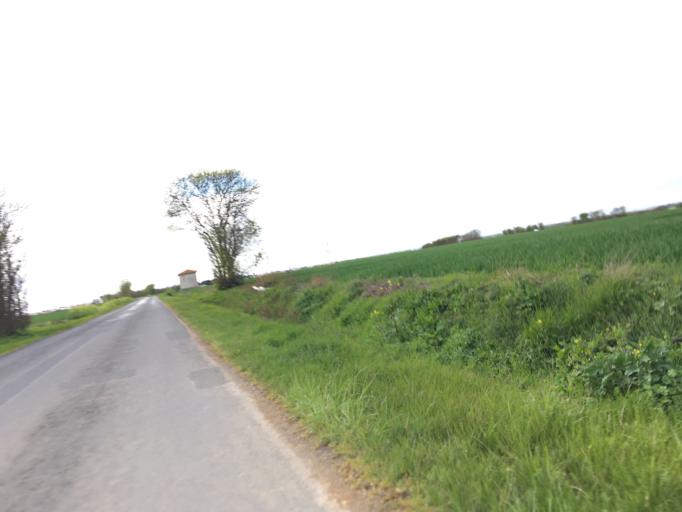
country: FR
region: Poitou-Charentes
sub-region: Departement de la Charente-Maritime
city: Saint-Rogatien
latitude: 46.1454
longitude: -1.0472
